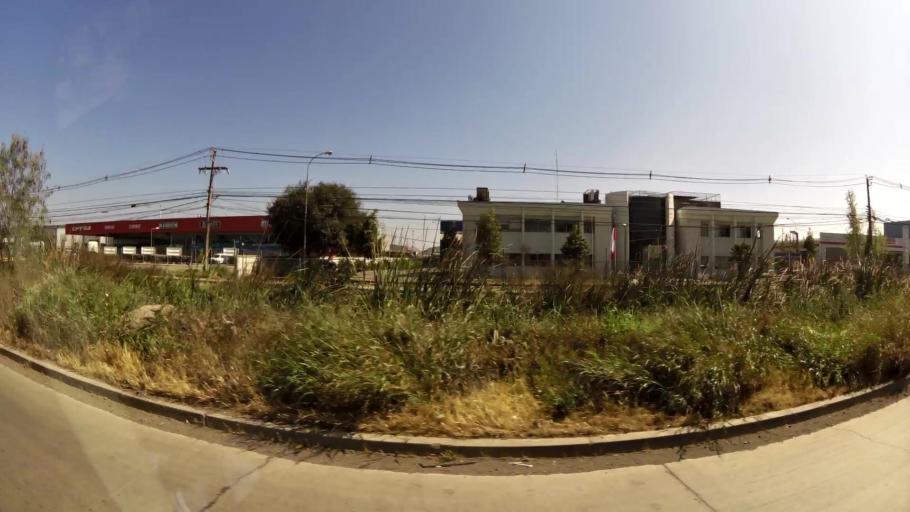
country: CL
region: Santiago Metropolitan
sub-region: Provincia de Chacabuco
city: Chicureo Abajo
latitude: -33.3174
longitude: -70.7314
